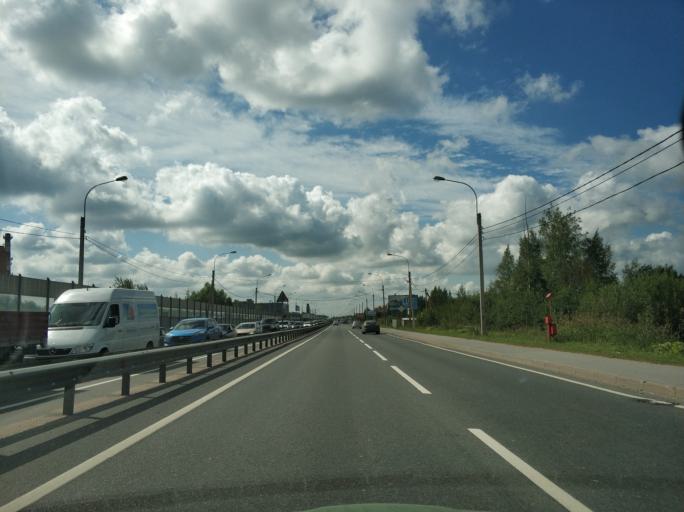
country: RU
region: Leningrad
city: Vsevolozhsk
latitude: 60.0303
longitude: 30.6245
